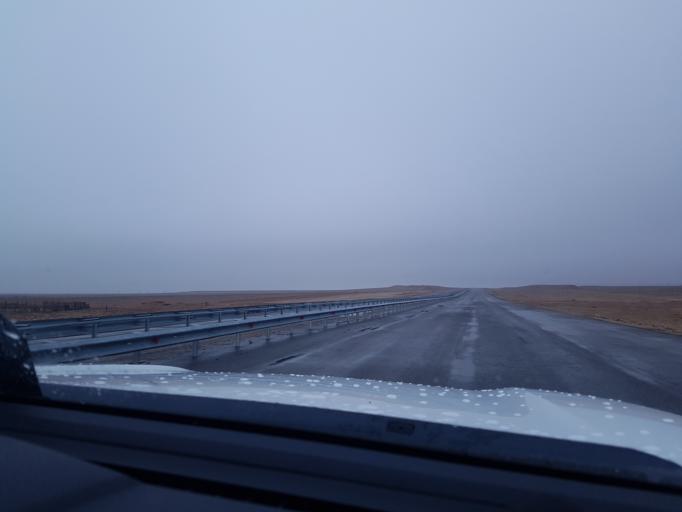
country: TM
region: Balkan
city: Balkanabat
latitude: 39.9665
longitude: 53.8090
